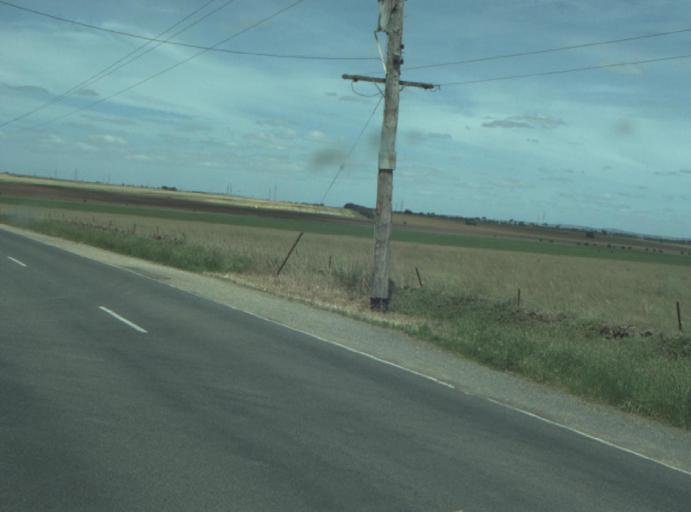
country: AU
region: Victoria
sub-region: Greater Geelong
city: Bell Post Hill
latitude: -38.0109
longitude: 144.2847
